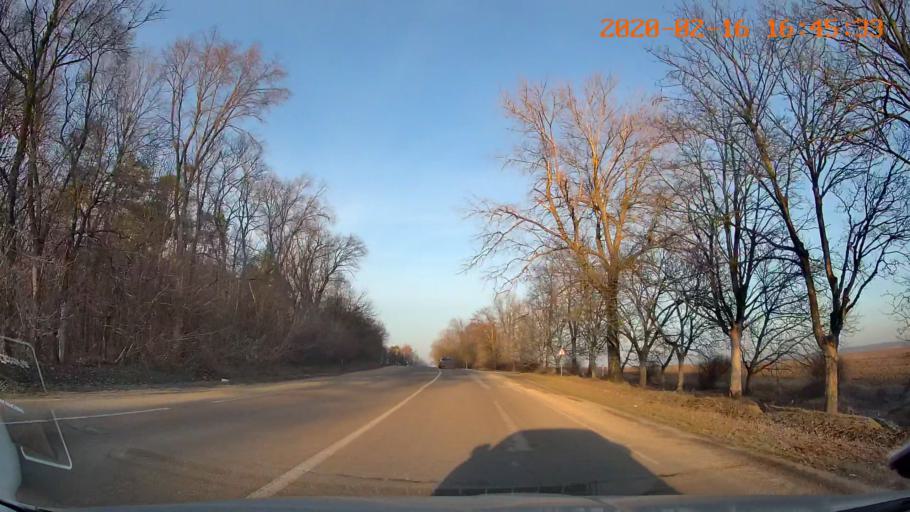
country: RO
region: Botosani
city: Radauti
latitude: 48.2778
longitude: 26.8345
